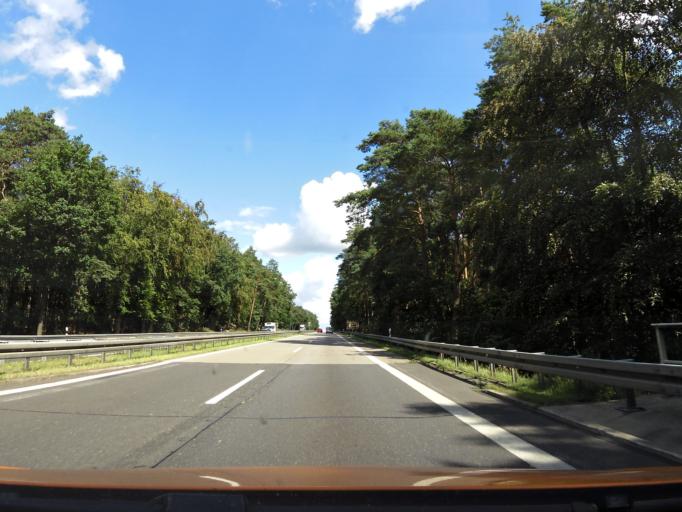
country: DE
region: Brandenburg
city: Britz
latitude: 52.9058
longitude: 13.7428
